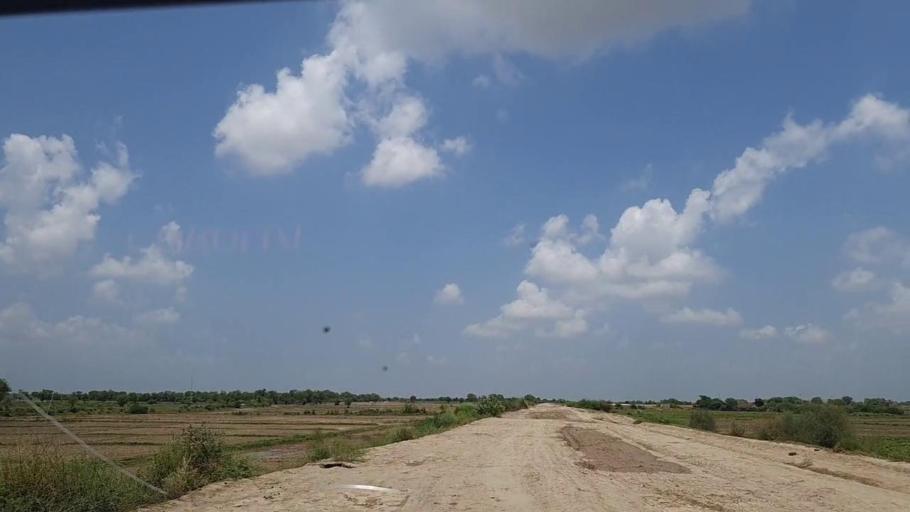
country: PK
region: Sindh
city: Tharu Shah
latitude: 26.9432
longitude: 68.0134
